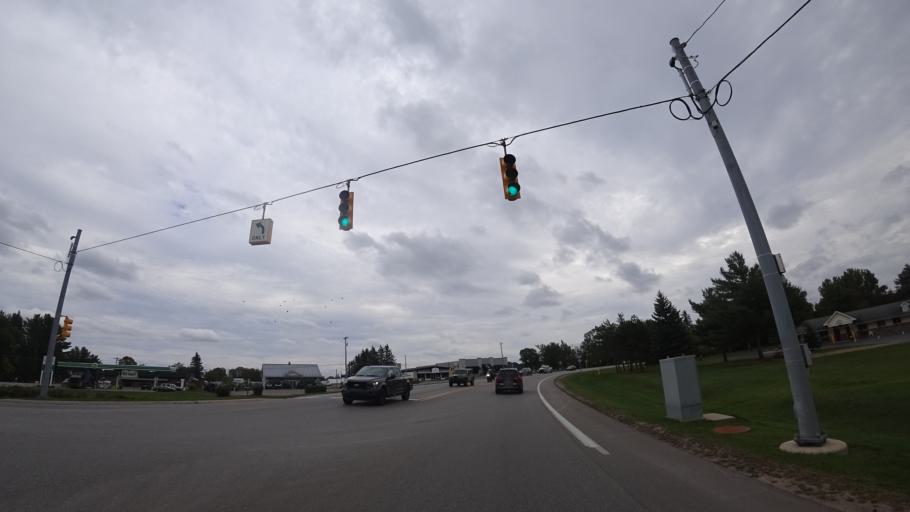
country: US
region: Michigan
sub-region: Emmet County
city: Petoskey
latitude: 45.4275
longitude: -84.9057
